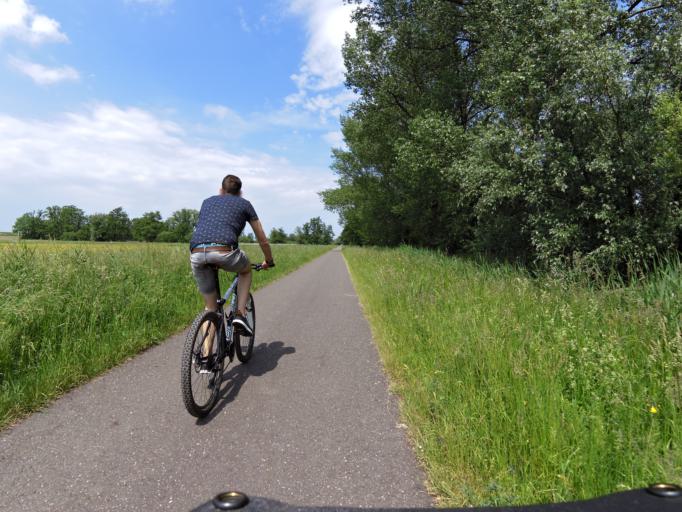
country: NL
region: North Brabant
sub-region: Gemeente Woudrichem
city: Woudrichem
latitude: 51.8025
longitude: 5.0606
